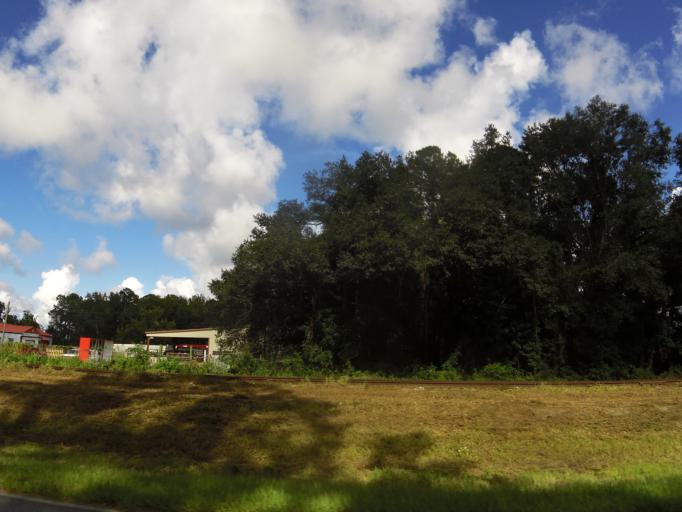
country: US
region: Georgia
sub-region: Camden County
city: Kingsland
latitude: 30.8072
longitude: -81.6929
